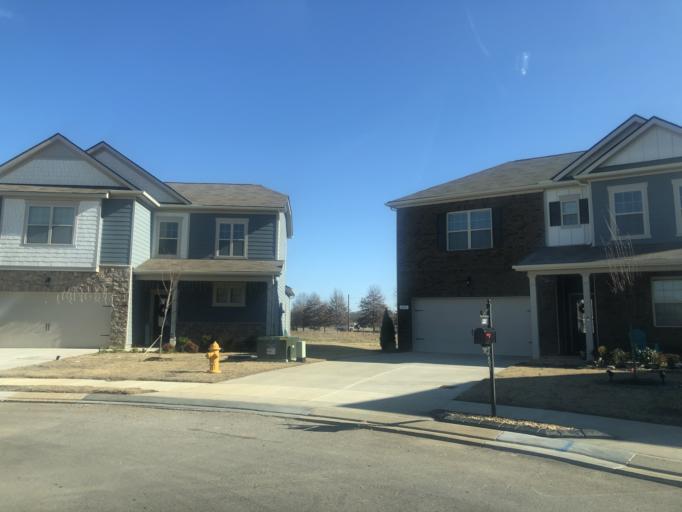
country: US
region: Tennessee
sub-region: Rutherford County
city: Smyrna
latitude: 35.9388
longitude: -86.5321
